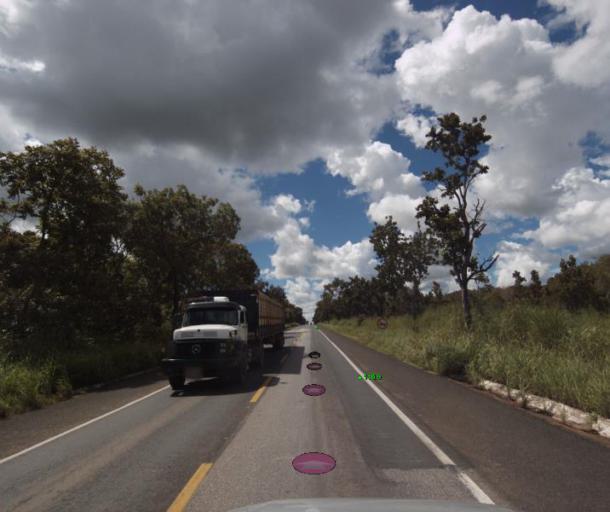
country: BR
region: Goias
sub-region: Porangatu
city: Porangatu
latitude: -13.7987
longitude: -49.0365
